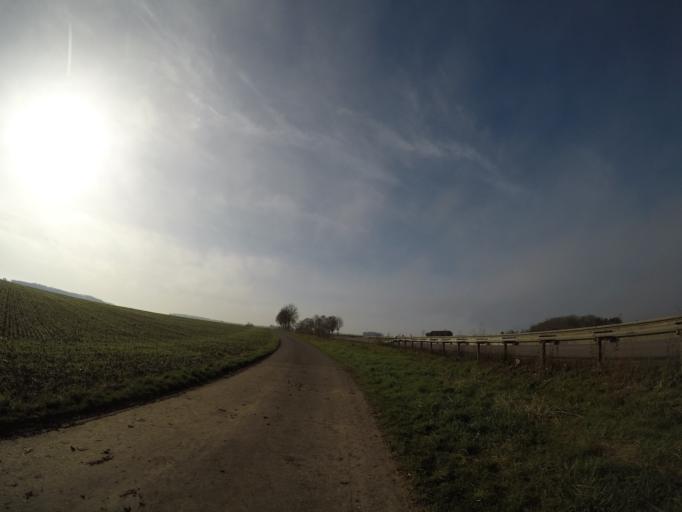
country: DE
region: Baden-Wuerttemberg
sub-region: Tuebingen Region
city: Langenau
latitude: 48.4906
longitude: 10.0747
